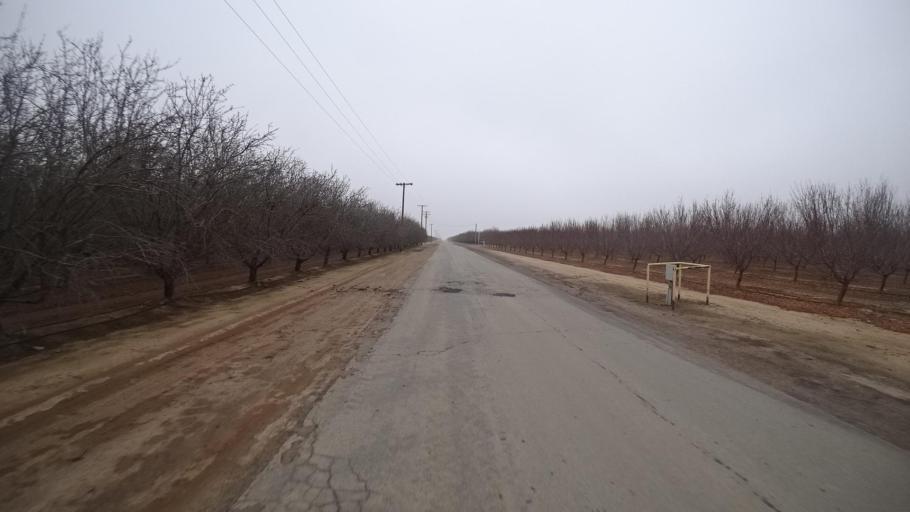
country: US
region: California
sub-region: Kern County
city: Wasco
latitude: 35.5659
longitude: -119.4919
